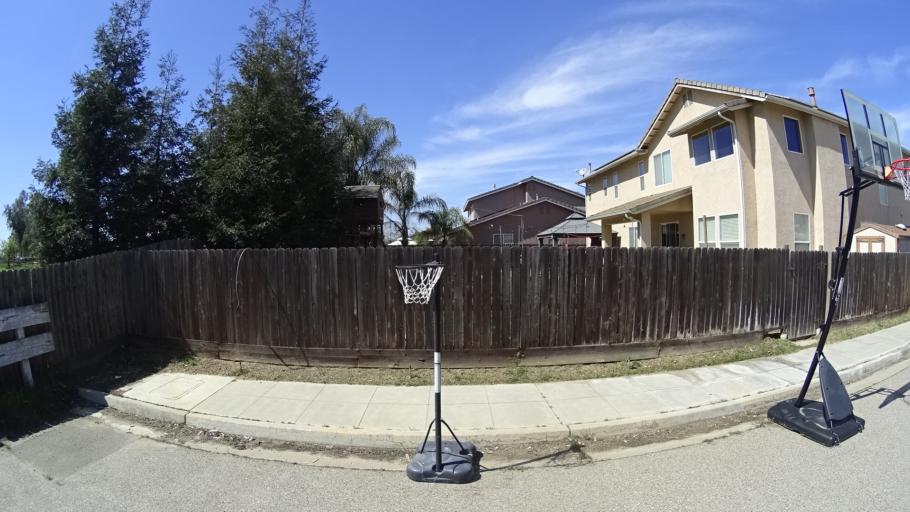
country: US
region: California
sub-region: Fresno County
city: Biola
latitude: 36.8170
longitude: -119.9118
